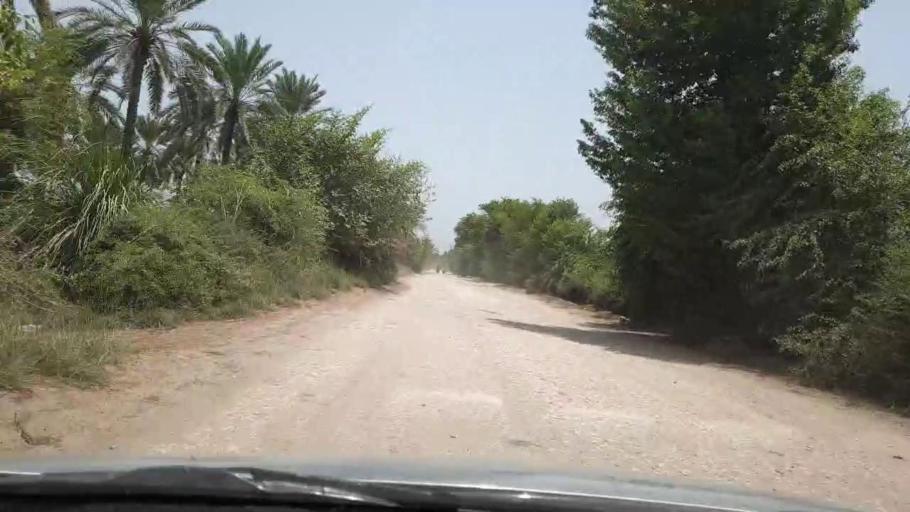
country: PK
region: Sindh
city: Pano Aqil
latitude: 27.8594
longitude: 69.0910
